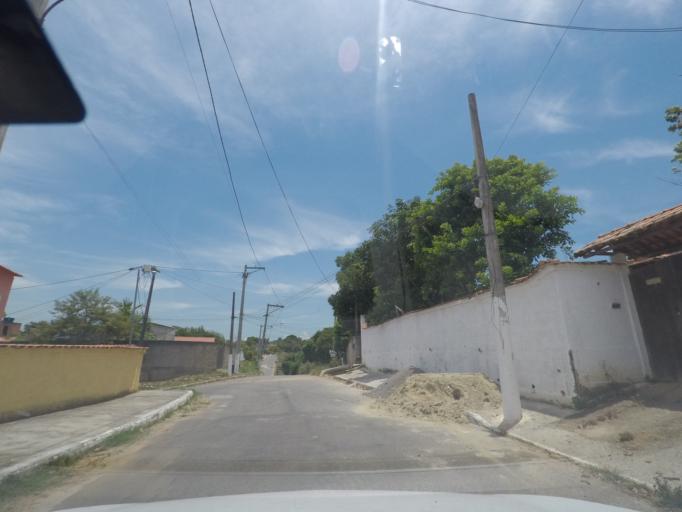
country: BR
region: Rio de Janeiro
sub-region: Marica
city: Marica
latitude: -22.9311
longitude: -42.8253
